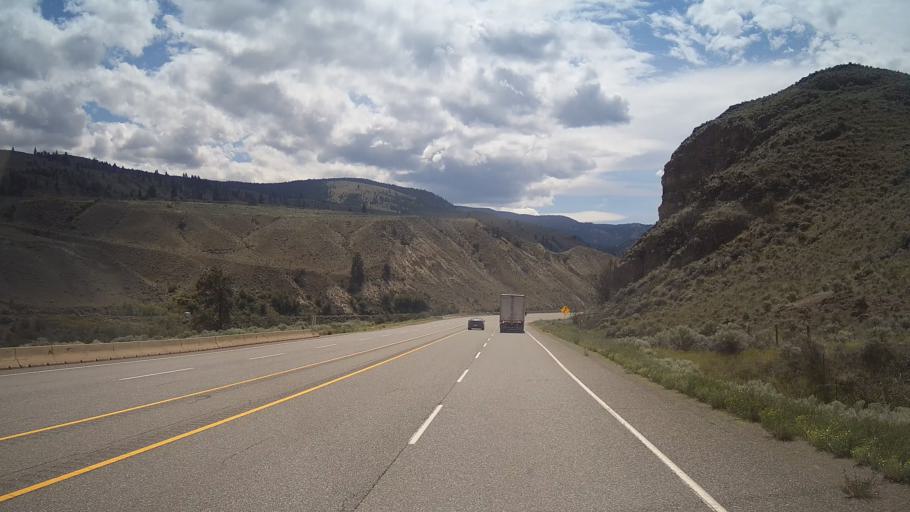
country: CA
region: British Columbia
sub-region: Thompson-Nicola Regional District
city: Ashcroft
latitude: 50.5149
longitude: -121.2830
